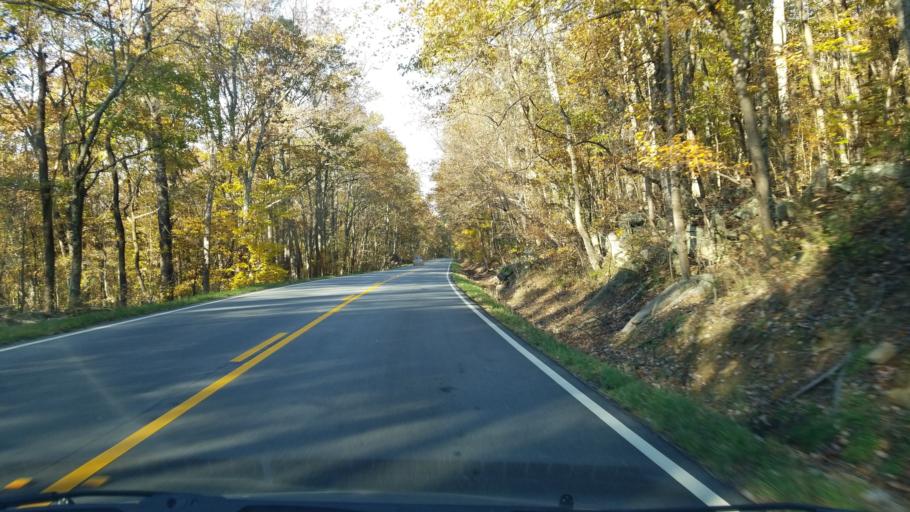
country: US
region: Georgia
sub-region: Dade County
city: Trenton
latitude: 34.8356
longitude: -85.5003
